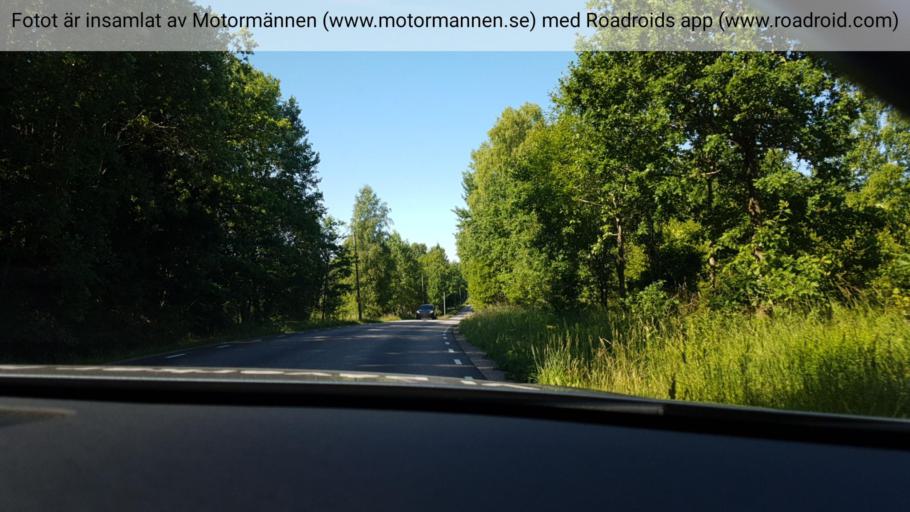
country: SE
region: Vaestra Goetaland
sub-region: Ulricehamns Kommun
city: Ulricehamn
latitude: 57.8438
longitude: 13.3833
